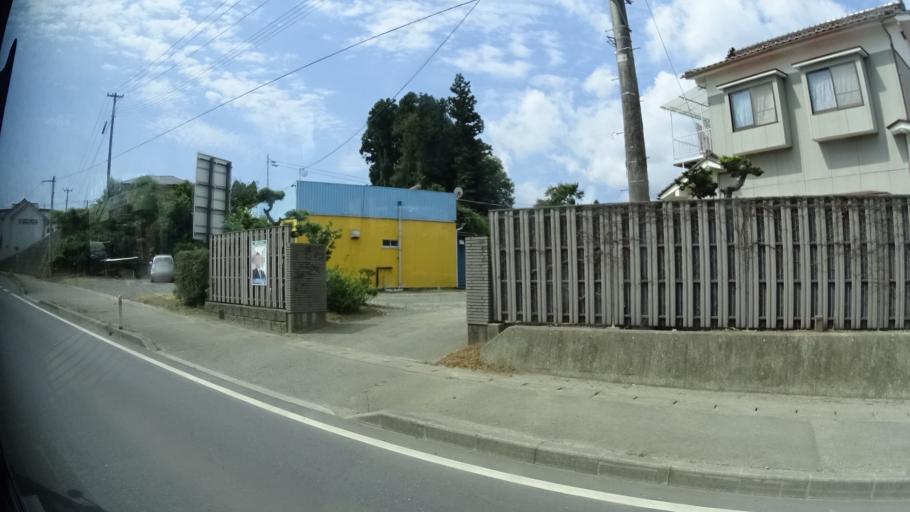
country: JP
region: Iwate
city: Ofunato
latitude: 38.8806
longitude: 141.5758
